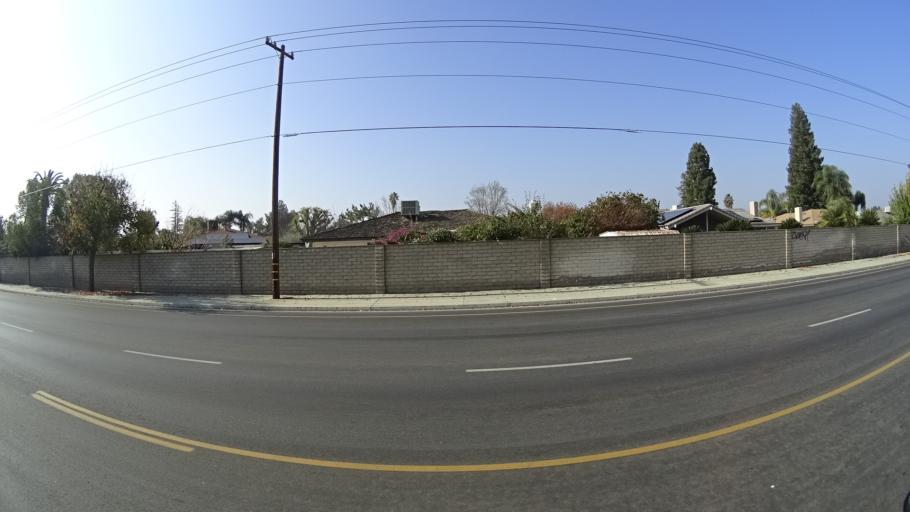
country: US
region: California
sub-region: Kern County
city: Greenacres
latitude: 35.3224
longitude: -119.0744
